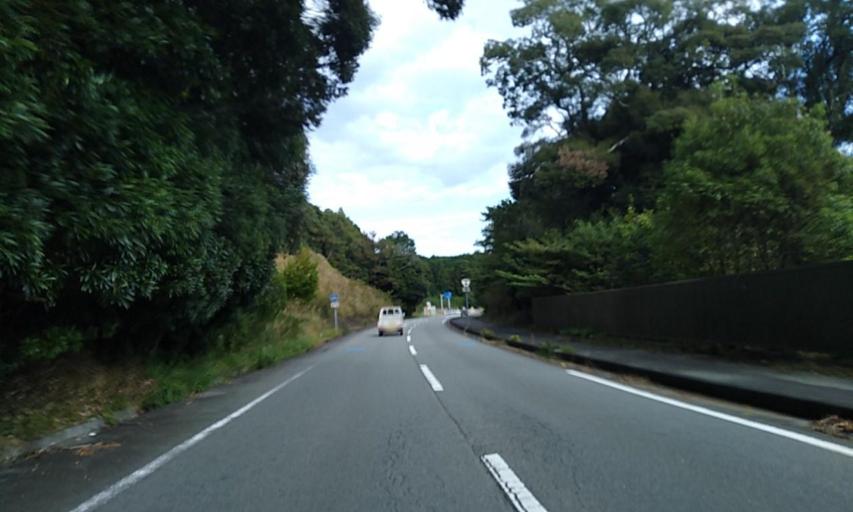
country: JP
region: Mie
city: Ise
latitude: 34.2900
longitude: 136.5662
